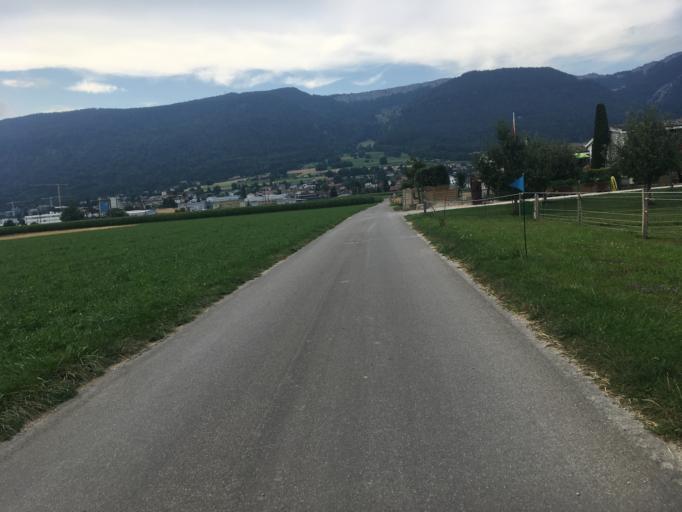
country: CH
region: Solothurn
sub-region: Bezirk Lebern
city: Bettlach
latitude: 47.1903
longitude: 7.4223
